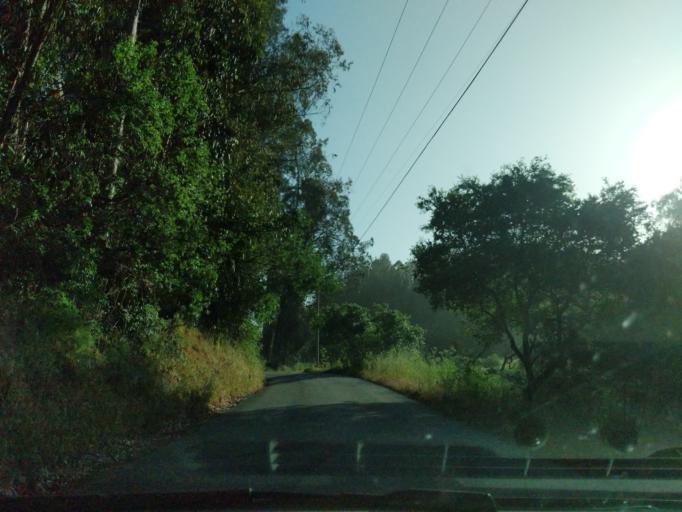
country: US
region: California
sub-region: Monterey County
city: Las Lomas
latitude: 36.8885
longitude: -121.7212
